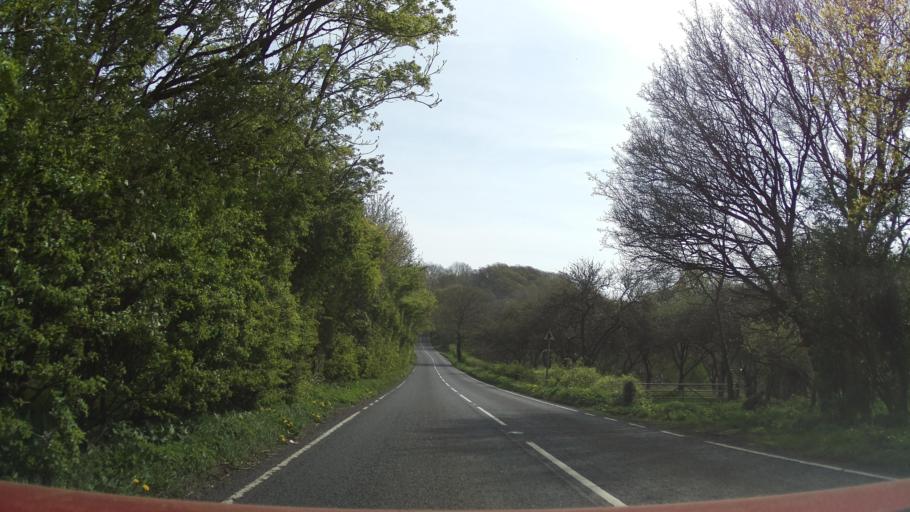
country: GB
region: England
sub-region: Somerset
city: Street
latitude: 51.1104
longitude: -2.7566
